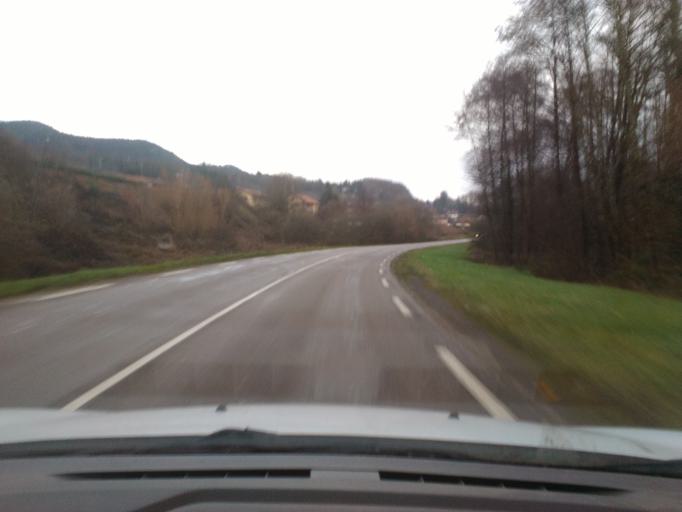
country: FR
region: Lorraine
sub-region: Departement des Vosges
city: Moyenmoutier
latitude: 48.3828
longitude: 6.9338
